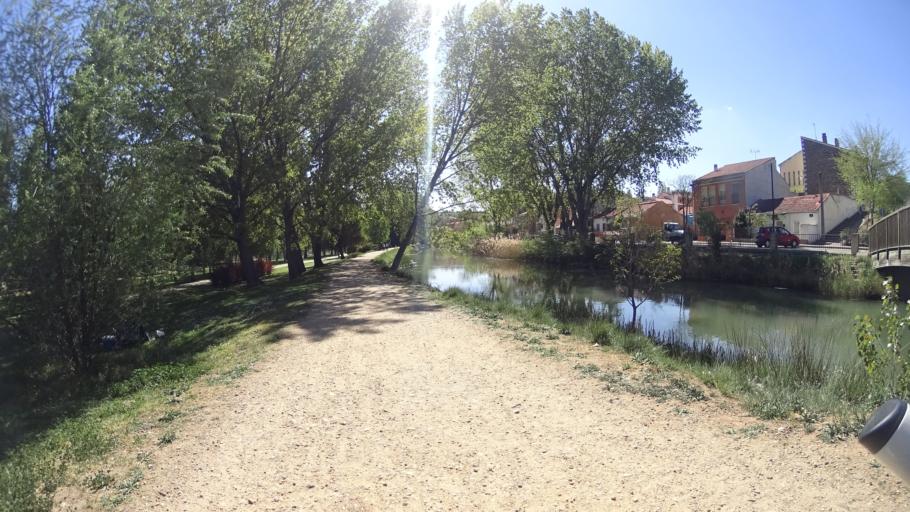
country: ES
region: Castille and Leon
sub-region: Provincia de Valladolid
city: Valladolid
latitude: 41.6698
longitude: -4.7340
